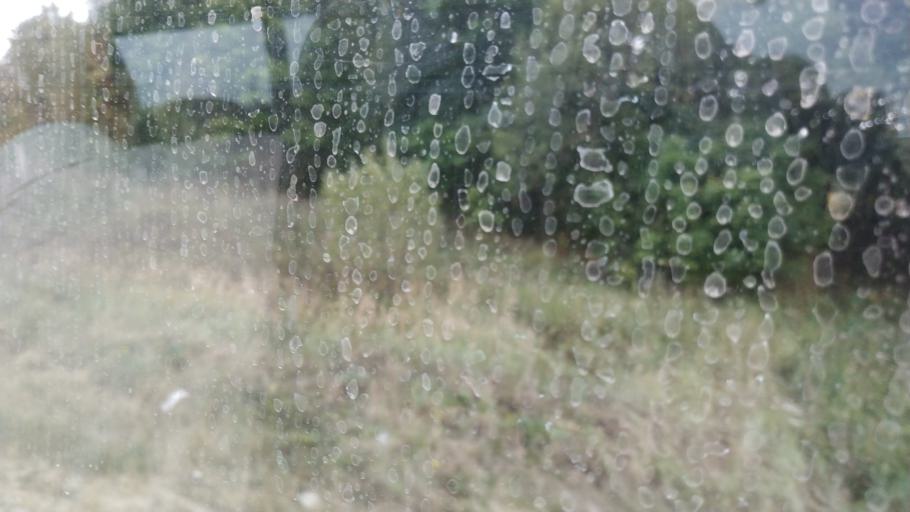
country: RU
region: Moskovskaya
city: Il'inskoye
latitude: 55.3286
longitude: 38.0824
